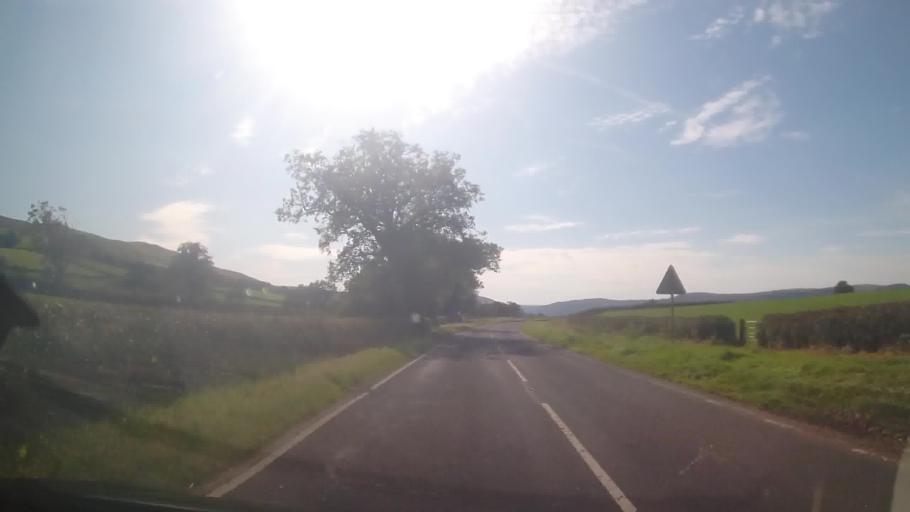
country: GB
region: Wales
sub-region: Sir Powys
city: Rhayader
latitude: 52.3048
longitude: -3.4851
